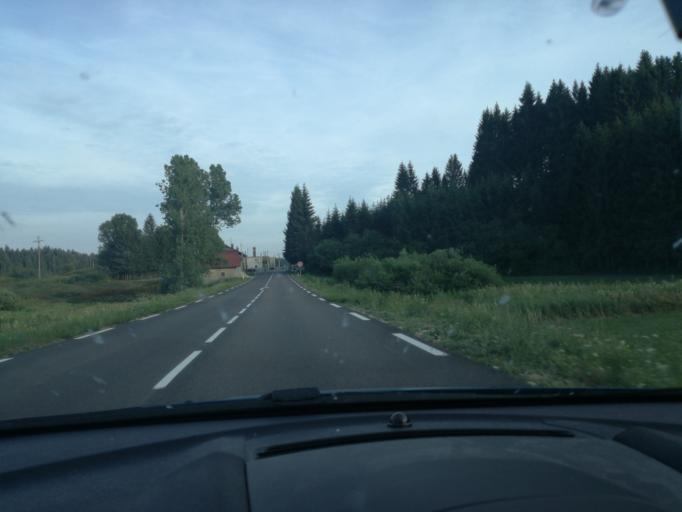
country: FR
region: Franche-Comte
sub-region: Departement du Jura
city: Morbier
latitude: 46.6102
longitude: 5.9608
